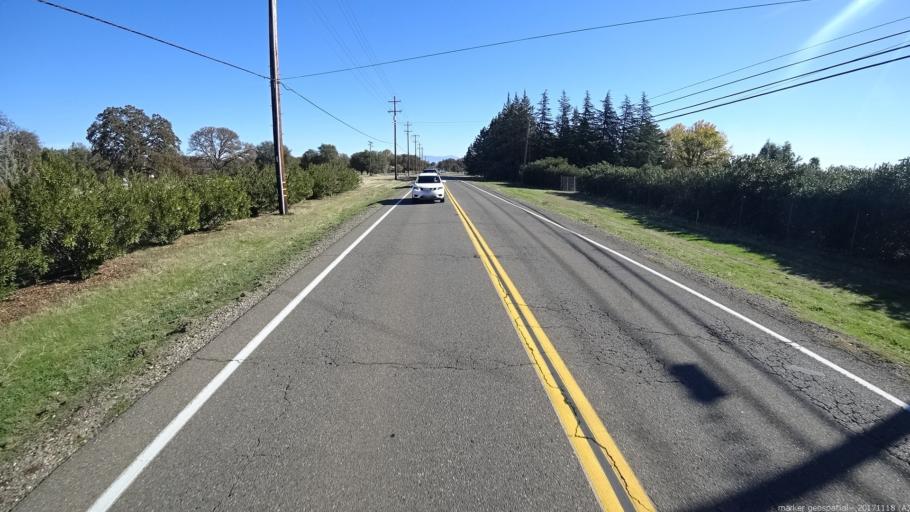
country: US
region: California
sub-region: Shasta County
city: Cottonwood
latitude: 40.3892
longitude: -122.3240
